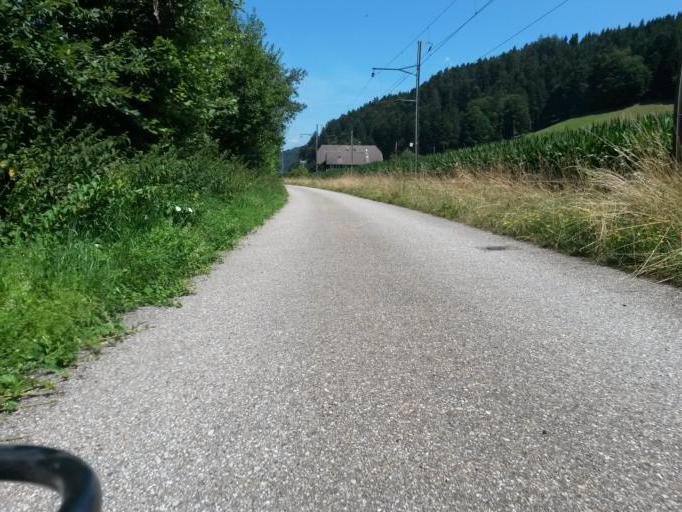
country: CH
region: Bern
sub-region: Bern-Mittelland District
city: Walkringen
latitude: 46.9779
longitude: 7.6389
